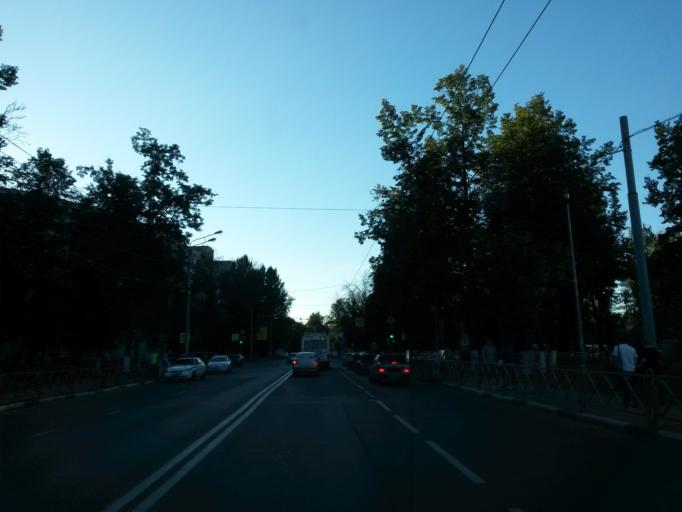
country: RU
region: Jaroslavl
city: Yaroslavl
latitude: 57.6352
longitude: 39.8823
